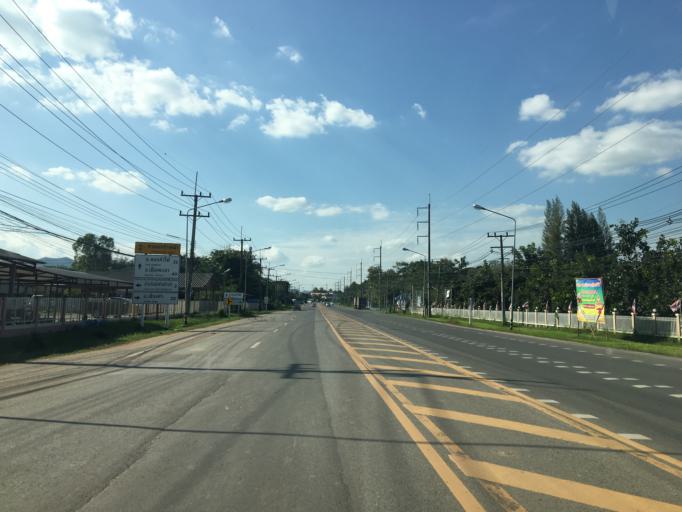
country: TH
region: Phayao
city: Chun
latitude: 19.3359
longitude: 100.1344
